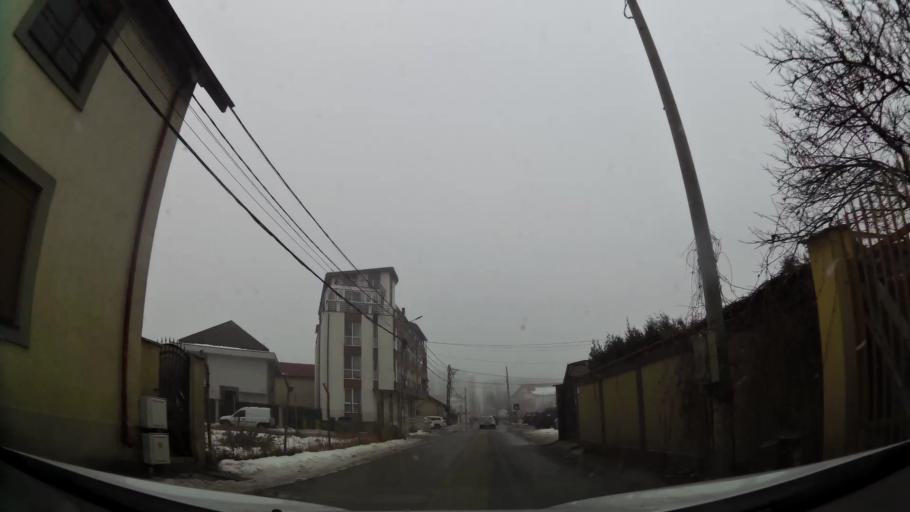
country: RO
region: Ilfov
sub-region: Comuna Chiajna
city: Rosu
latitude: 44.4502
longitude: 25.9924
